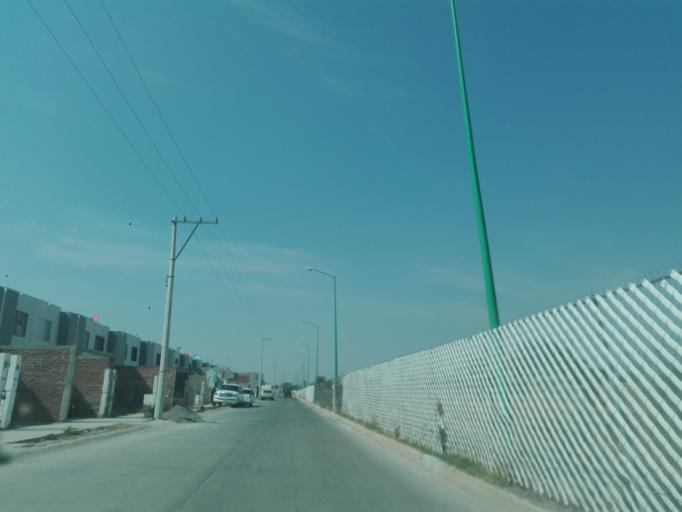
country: MX
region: Guanajuato
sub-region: Leon
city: Ladrilleras del Refugio
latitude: 21.0722
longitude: -101.5613
